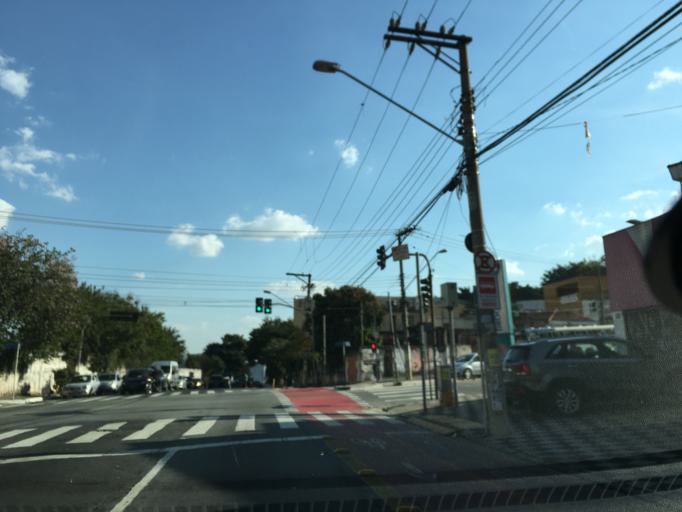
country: BR
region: Sao Paulo
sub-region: Sao Paulo
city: Sao Paulo
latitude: -23.4820
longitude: -46.6472
